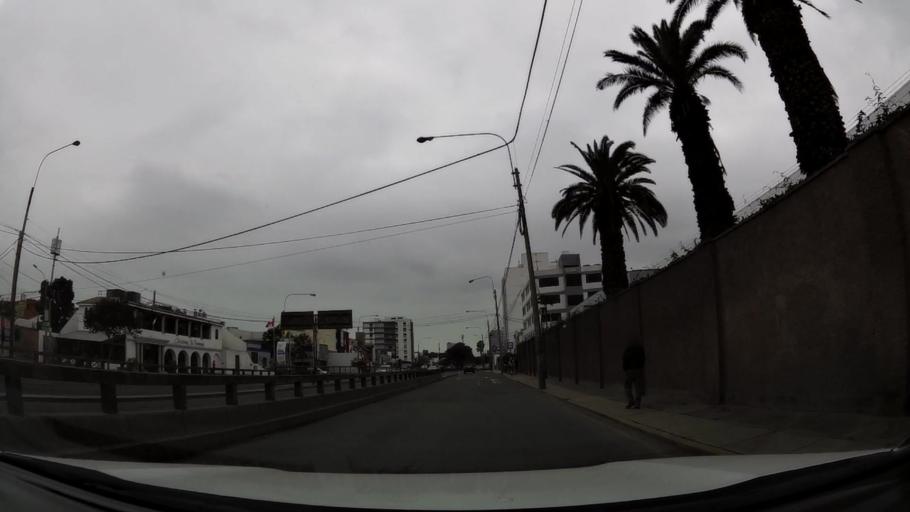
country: PE
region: Lima
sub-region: Lima
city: Surco
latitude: -12.1285
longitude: -77.0033
